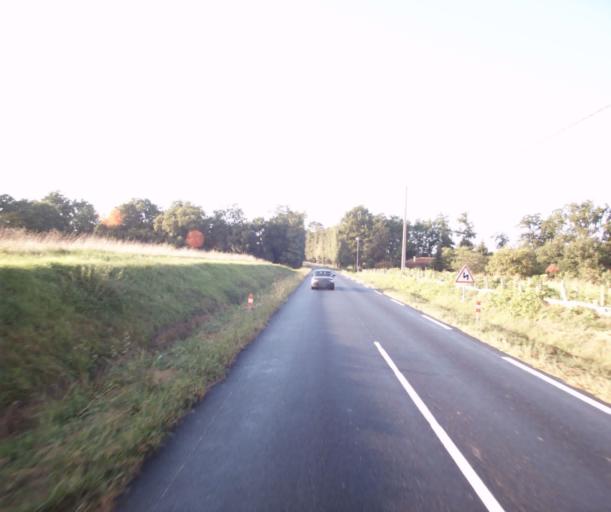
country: FR
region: Midi-Pyrenees
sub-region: Departement du Gers
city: Cazaubon
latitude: 43.9181
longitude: -0.0291
